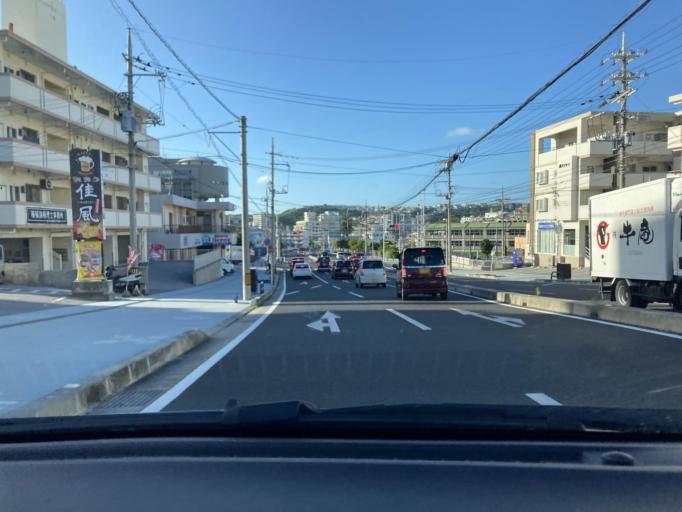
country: JP
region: Okinawa
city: Tomigusuku
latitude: 26.1902
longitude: 127.7302
